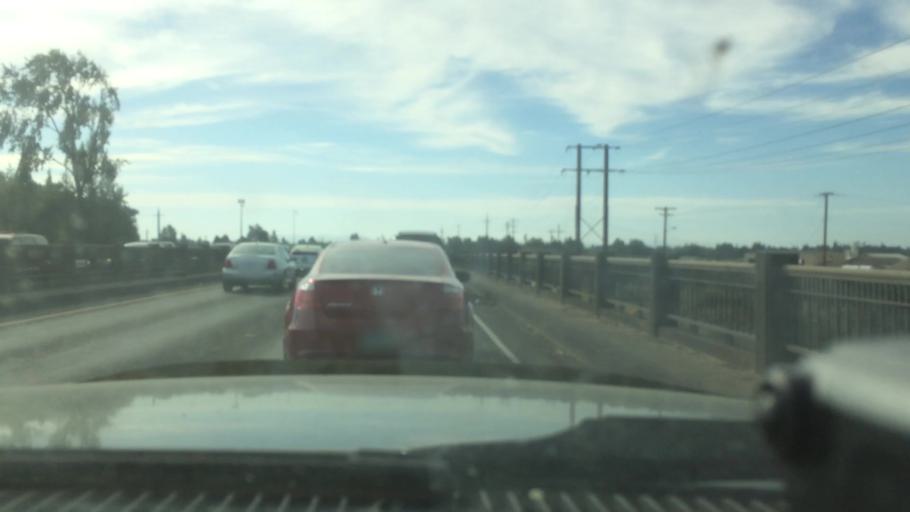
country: US
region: Oregon
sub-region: Lane County
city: Eugene
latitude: 44.0952
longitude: -123.1067
